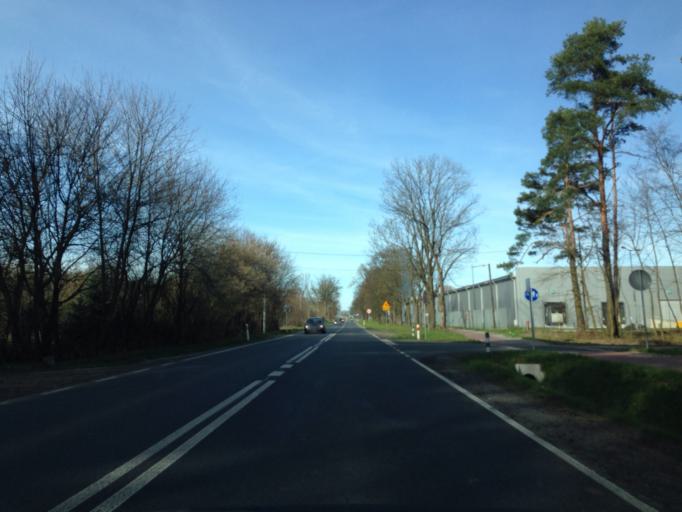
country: PL
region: Lodz Voivodeship
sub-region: Powiat poddebicki
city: Wartkowice
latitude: 51.9661
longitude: 19.0135
